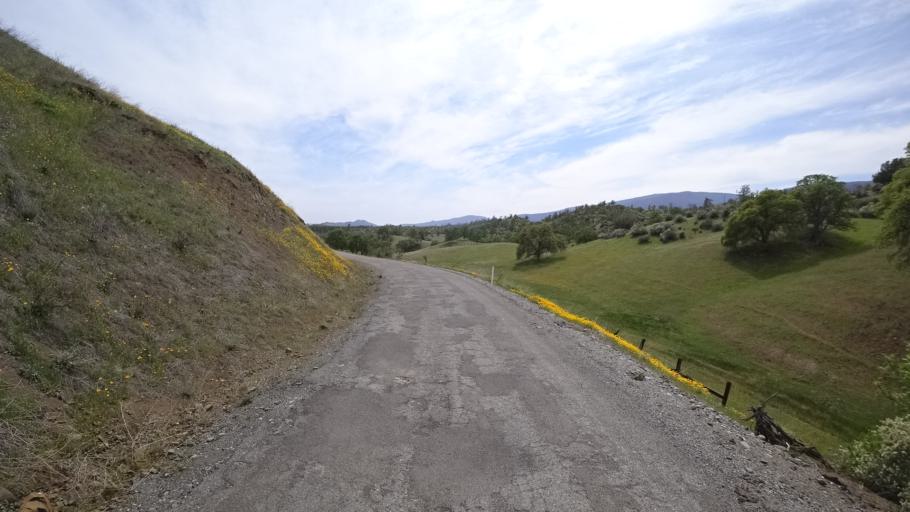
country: US
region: California
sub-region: Glenn County
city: Willows
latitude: 39.6189
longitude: -122.5919
